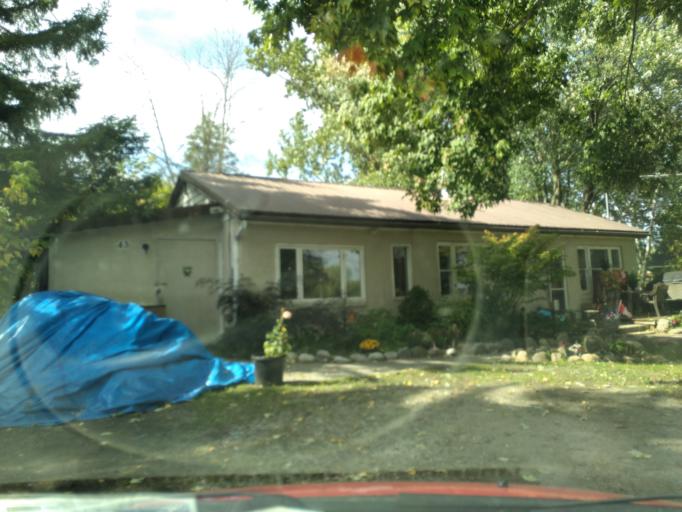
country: CA
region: Ontario
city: Keswick
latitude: 44.2997
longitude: -79.3640
